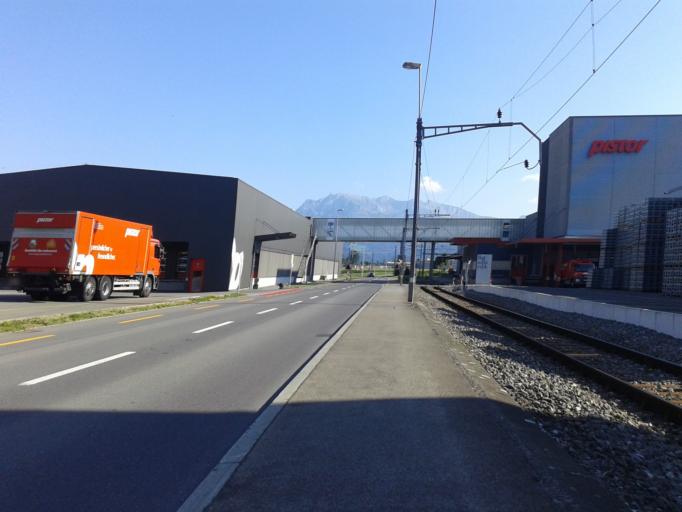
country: CH
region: Lucerne
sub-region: Sursee District
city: Neuenkirch
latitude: 47.0958
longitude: 8.2411
